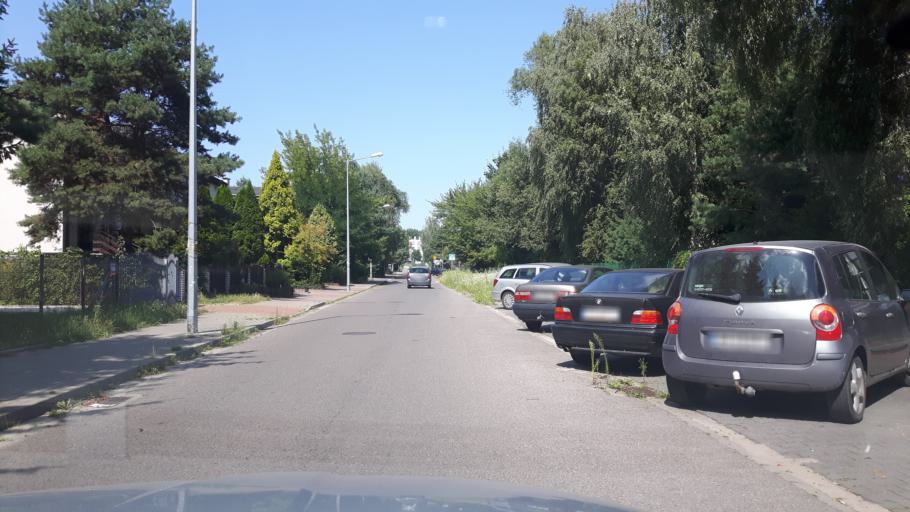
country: PL
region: Masovian Voivodeship
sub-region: Warszawa
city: Wesola
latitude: 52.2205
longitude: 21.2279
